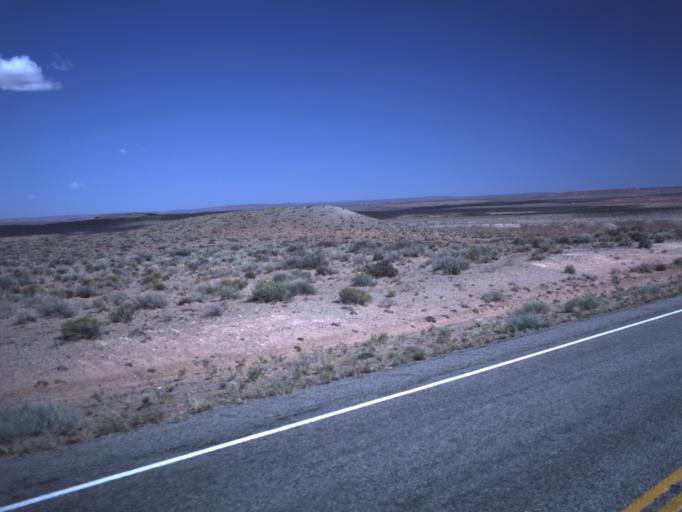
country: US
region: Utah
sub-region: Emery County
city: Ferron
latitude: 38.3359
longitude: -110.6857
